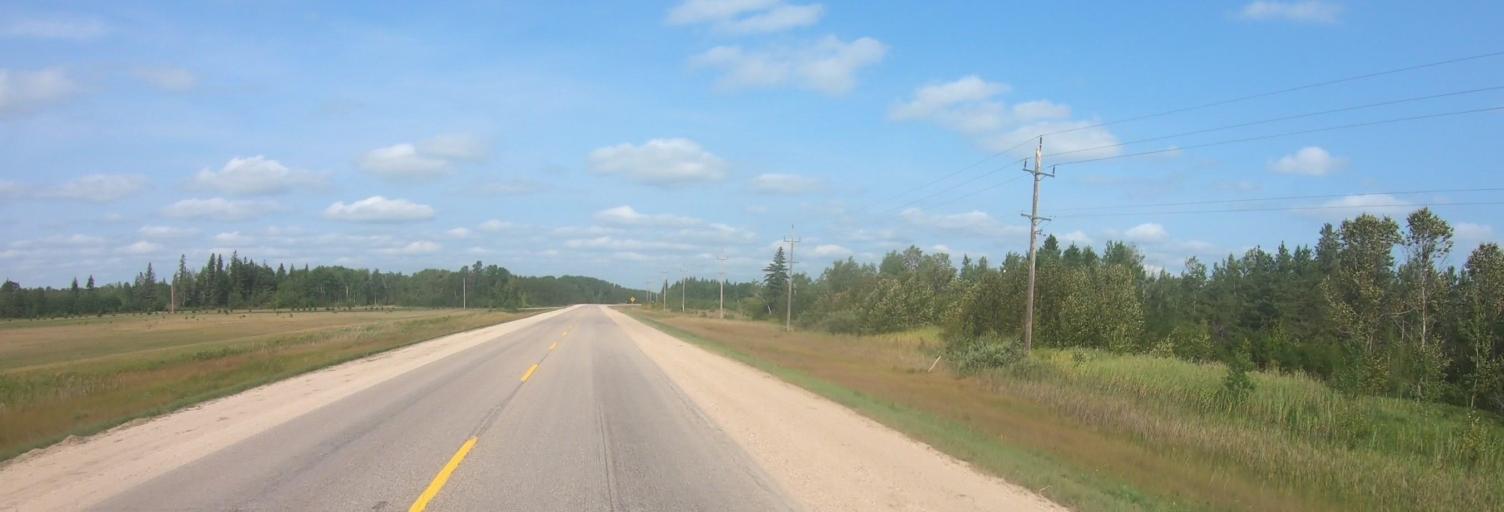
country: CA
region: Manitoba
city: La Broquerie
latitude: 49.1851
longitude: -96.2453
